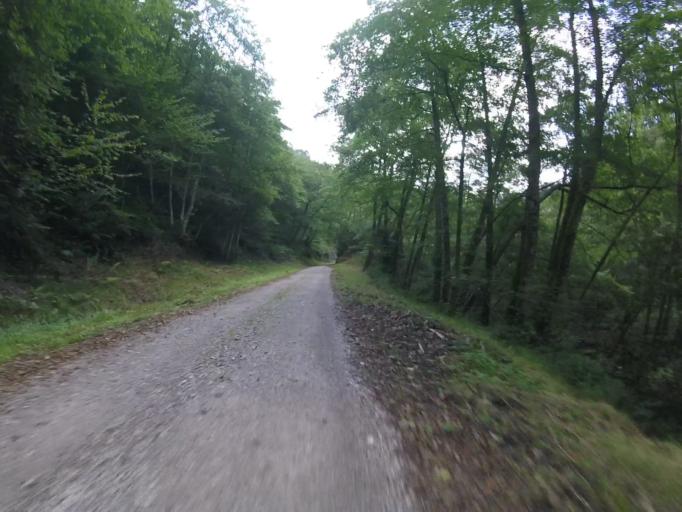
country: ES
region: Basque Country
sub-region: Provincia de Guipuzcoa
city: Elduayen
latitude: 43.1721
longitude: -1.9624
